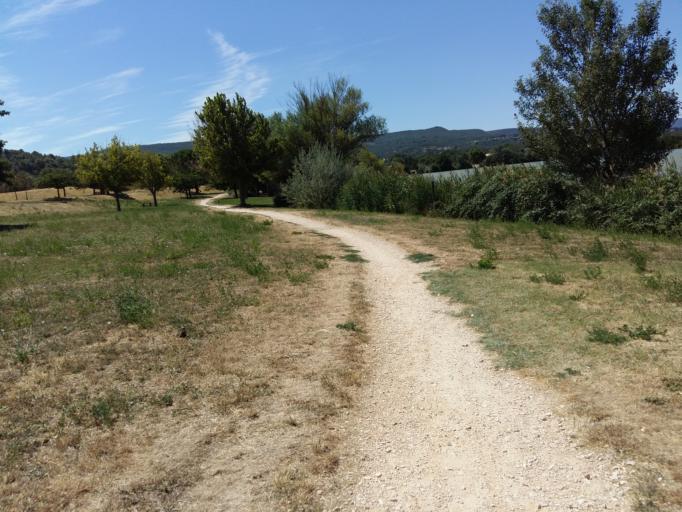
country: FR
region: Provence-Alpes-Cote d'Azur
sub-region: Departement du Vaucluse
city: Apt
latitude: 43.8918
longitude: 5.3805
